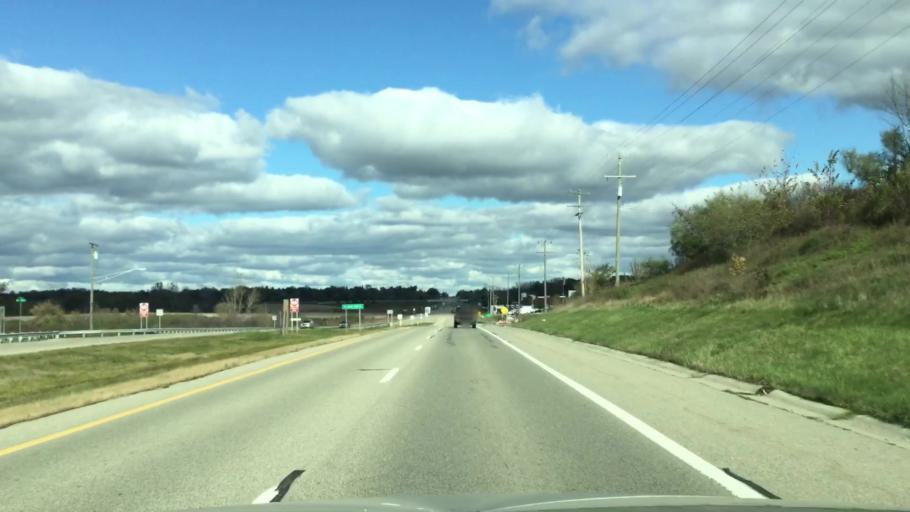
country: US
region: Michigan
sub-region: Lapeer County
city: Lapeer
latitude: 43.0127
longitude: -83.3218
